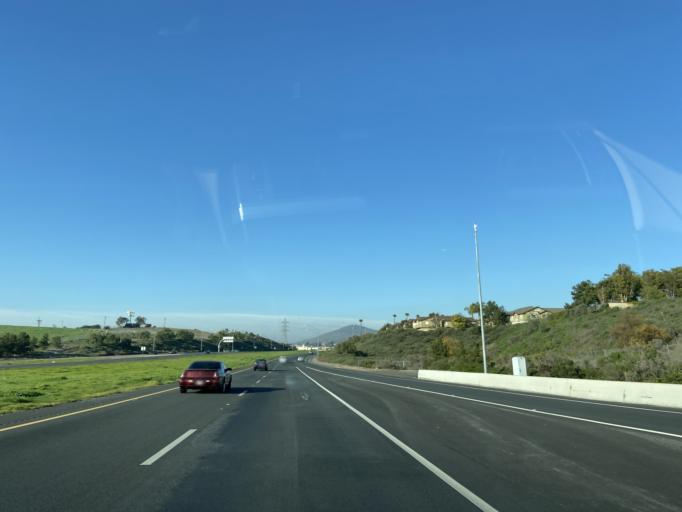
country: US
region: California
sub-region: San Diego County
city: Bonita
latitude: 32.6341
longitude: -116.9712
